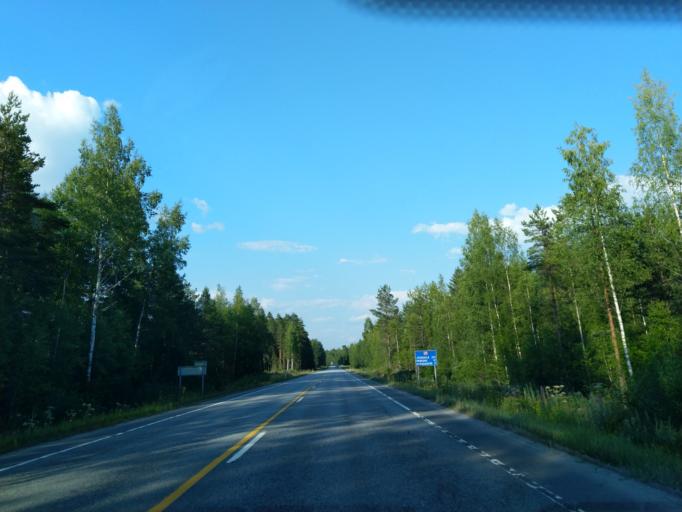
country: FI
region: Satakunta
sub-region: Pori
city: Laengelmaeki
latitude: 61.7508
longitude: 22.1147
